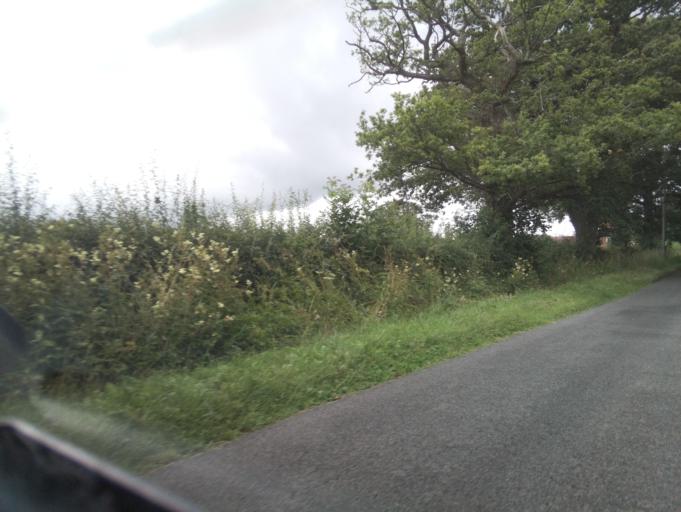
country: GB
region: England
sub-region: Solihull
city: Dickens Heath
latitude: 52.3745
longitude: -1.8379
